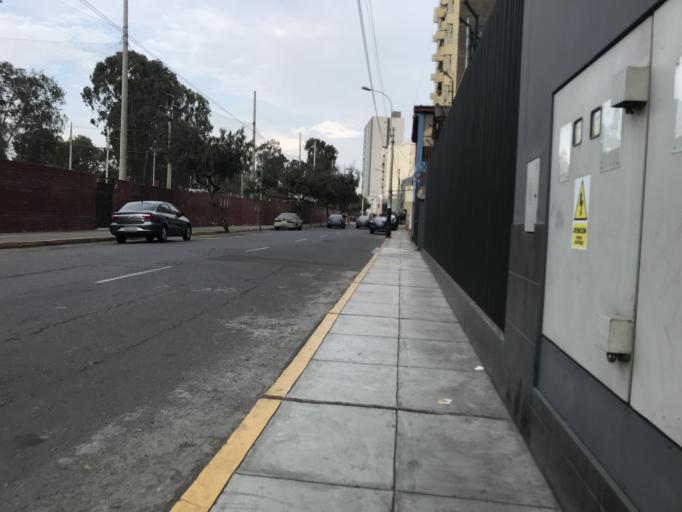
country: PE
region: Lima
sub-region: Lima
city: San Isidro
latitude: -12.0832
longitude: -77.0449
